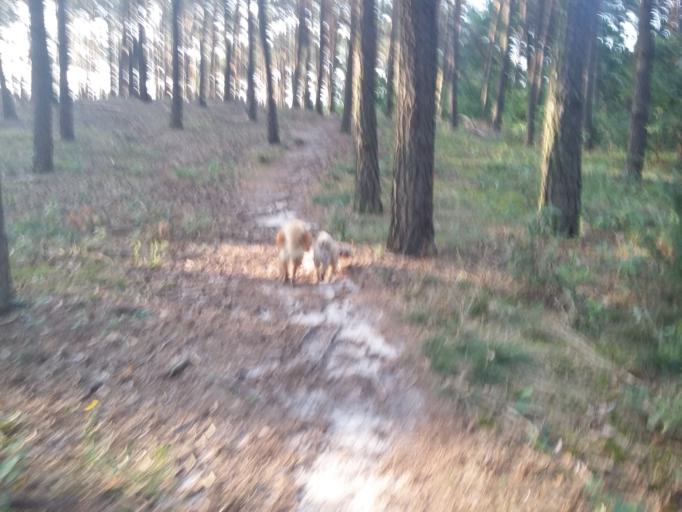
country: PL
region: Lodz Voivodeship
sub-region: Powiat pabianicki
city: Dobron
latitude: 51.5900
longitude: 19.2258
